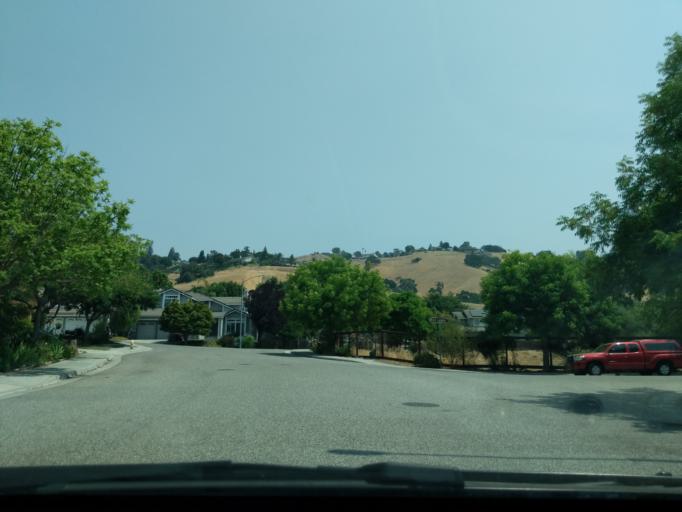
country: US
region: California
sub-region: Santa Clara County
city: San Martin
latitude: 37.1332
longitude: -121.6008
